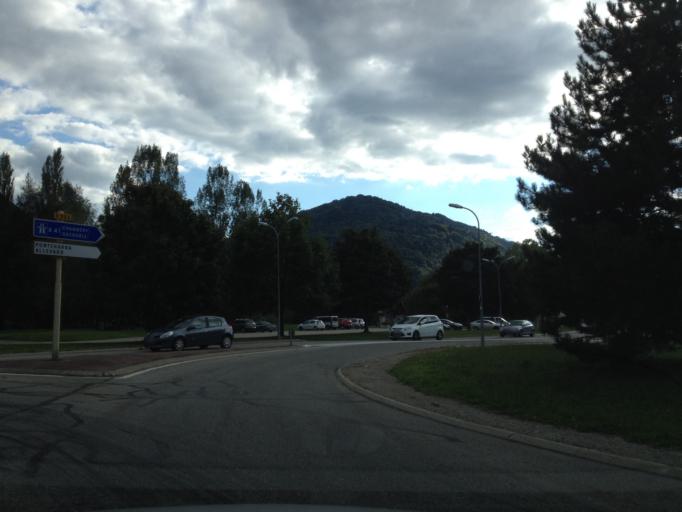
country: FR
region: Rhone-Alpes
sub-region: Departement de la Savoie
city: La Rochette
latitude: 45.4529
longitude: 6.1029
